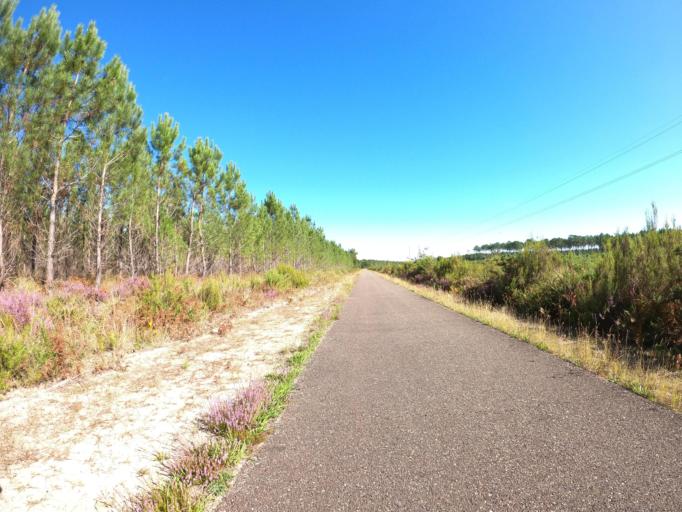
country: FR
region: Aquitaine
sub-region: Departement des Landes
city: Ychoux
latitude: 44.3404
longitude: -0.9746
